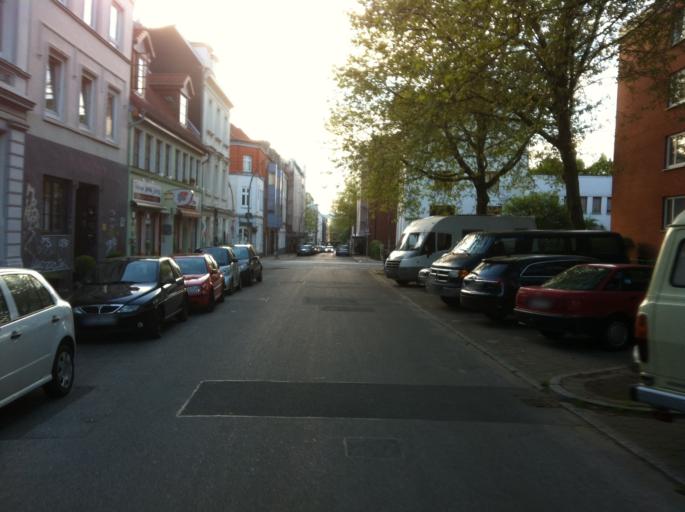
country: DE
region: Hamburg
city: St. Pauli
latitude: 53.5570
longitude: 9.9576
